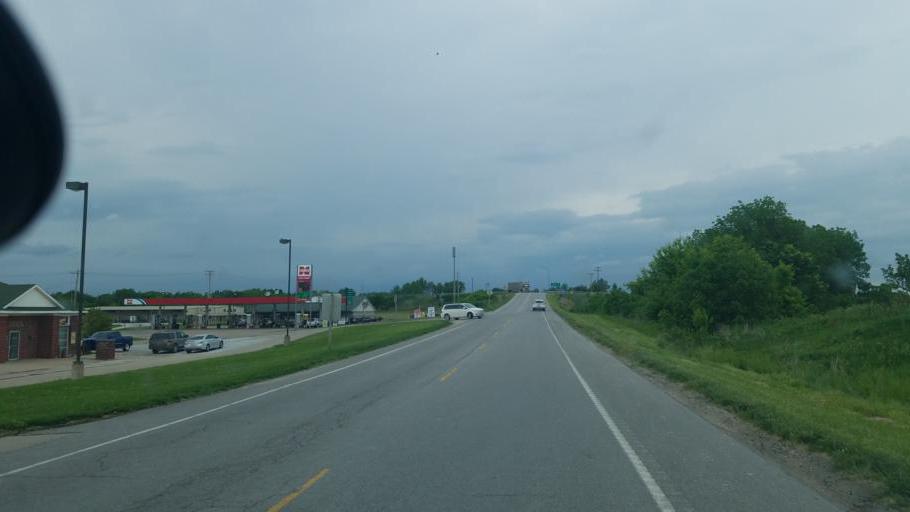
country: US
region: Missouri
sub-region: Cooper County
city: Boonville
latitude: 38.9344
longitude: -92.6906
